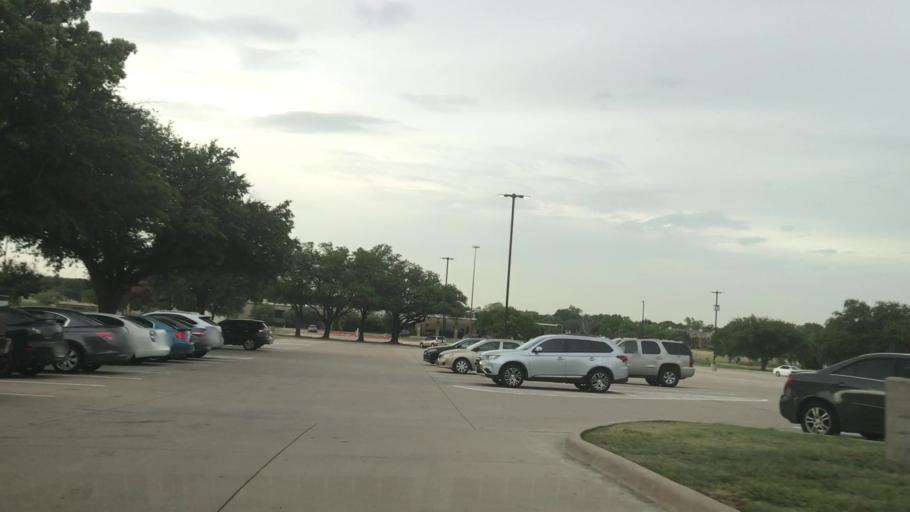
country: US
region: Texas
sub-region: Dallas County
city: Mesquite
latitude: 32.8167
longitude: -96.6585
